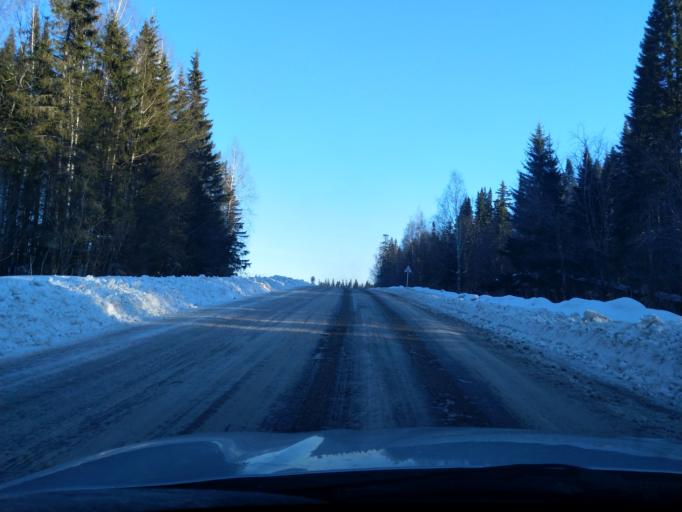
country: RU
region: Perm
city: Polazna
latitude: 58.2973
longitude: 56.4769
